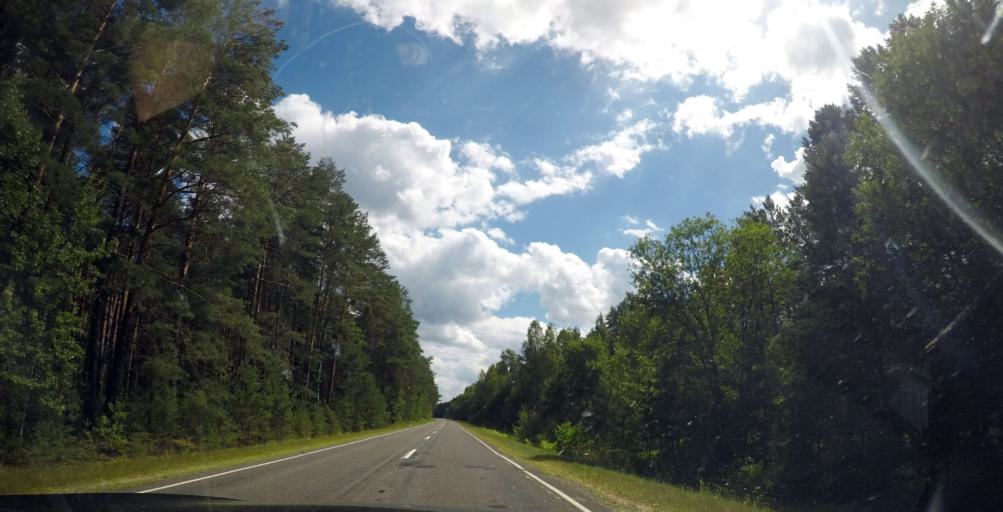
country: BY
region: Grodnenskaya
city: Skidal'
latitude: 53.8537
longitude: 24.1903
